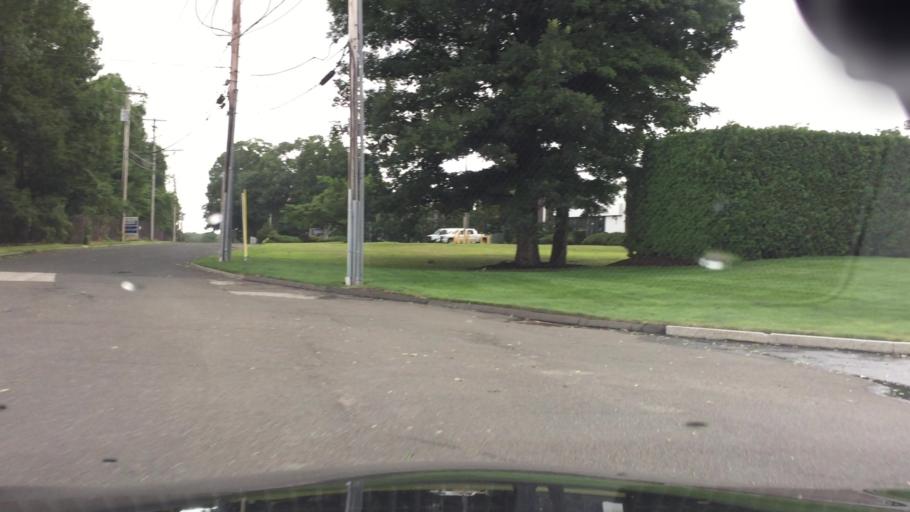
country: US
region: Connecticut
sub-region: Fairfield County
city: Shelton
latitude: 41.2741
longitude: -73.1286
